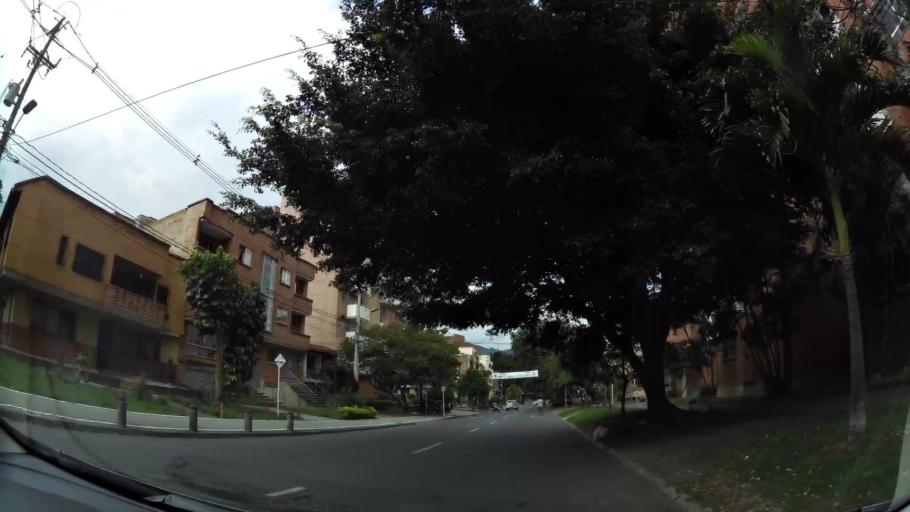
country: CO
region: Antioquia
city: Medellin
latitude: 6.2520
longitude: -75.5919
